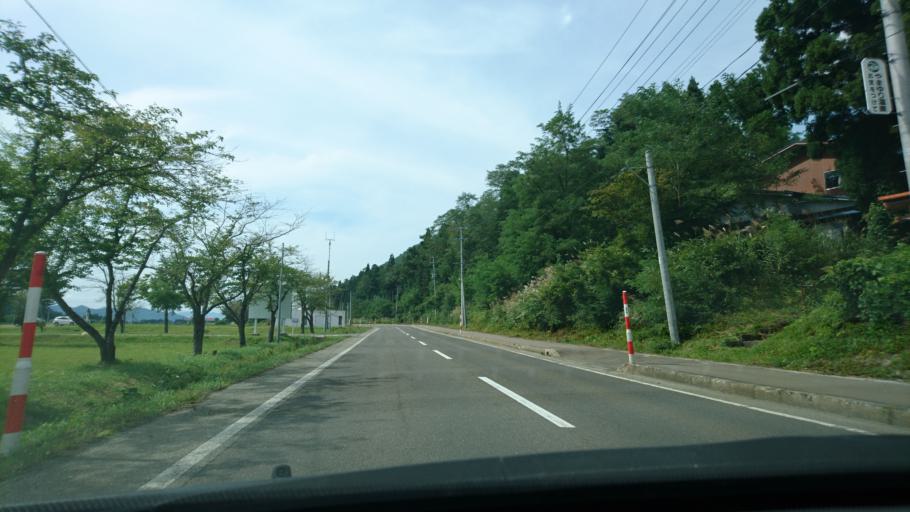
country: JP
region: Akita
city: Yuzawa
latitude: 39.2000
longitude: 140.5999
